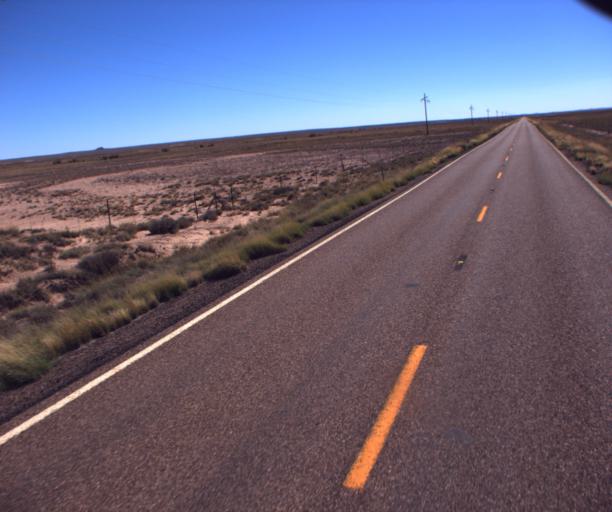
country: US
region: Arizona
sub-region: Navajo County
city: Holbrook
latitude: 35.1271
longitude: -110.0918
